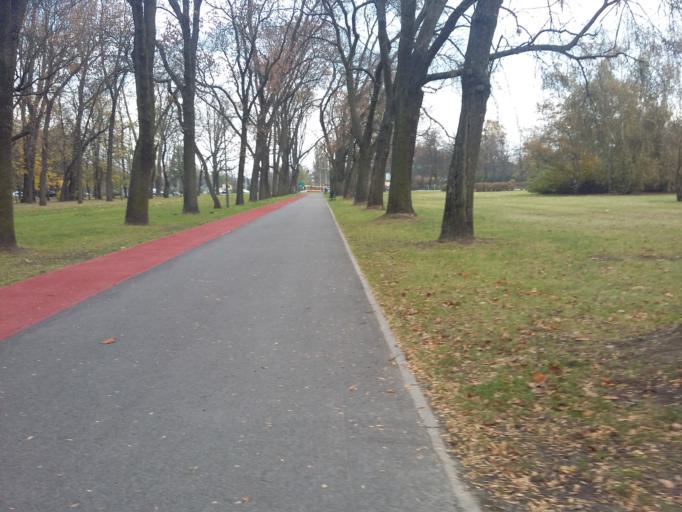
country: PL
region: Lodz Voivodeship
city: Lodz
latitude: 51.7655
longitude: 19.4203
